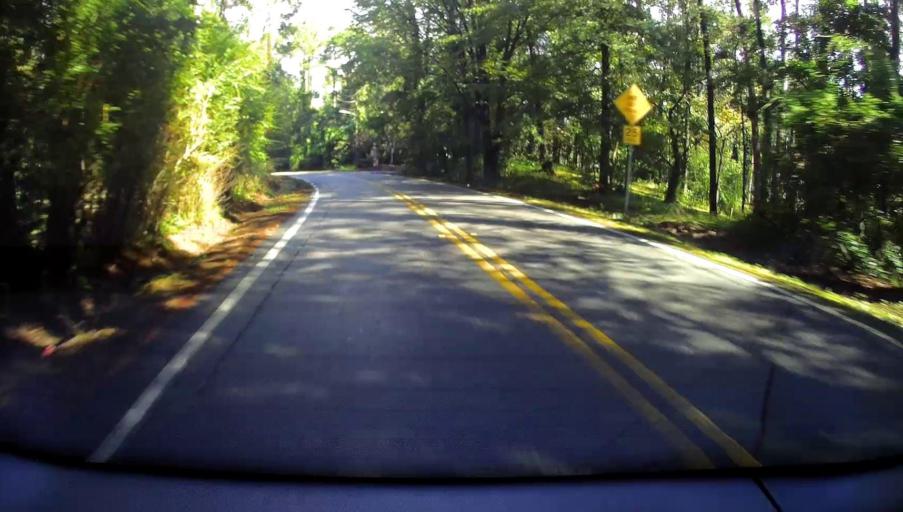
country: US
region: Georgia
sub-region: Bibb County
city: Macon
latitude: 32.8813
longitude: -83.7176
